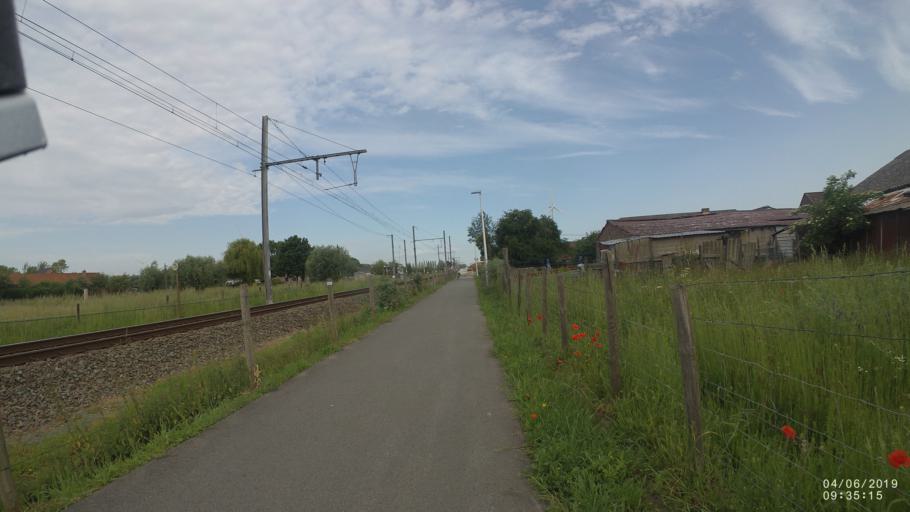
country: BE
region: Flanders
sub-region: Provincie Oost-Vlaanderen
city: Zele
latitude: 51.0796
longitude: 4.0276
